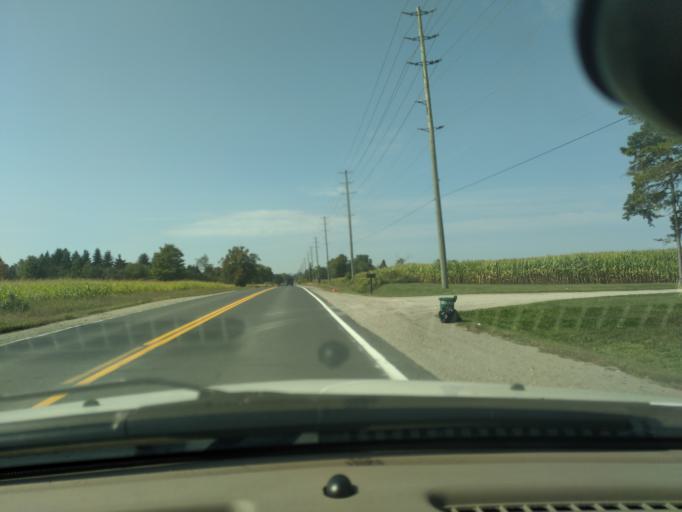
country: CA
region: Ontario
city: Innisfil
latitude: 44.2778
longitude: -79.7121
